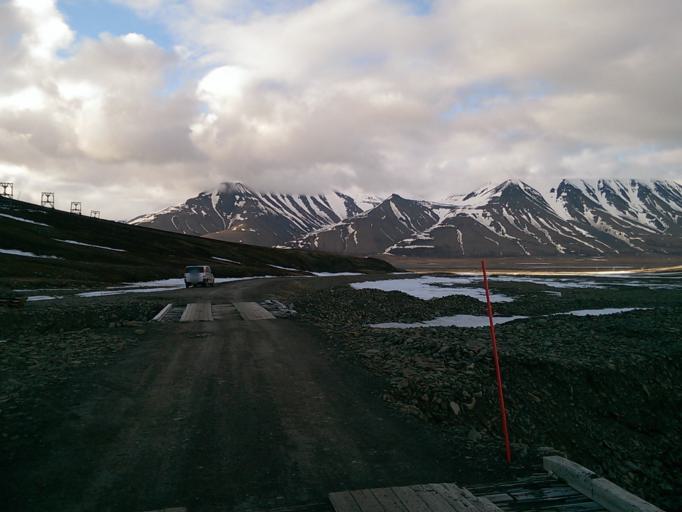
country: SJ
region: Svalbard
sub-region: Spitsbergen
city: Longyearbyen
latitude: 78.1853
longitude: 15.7622
